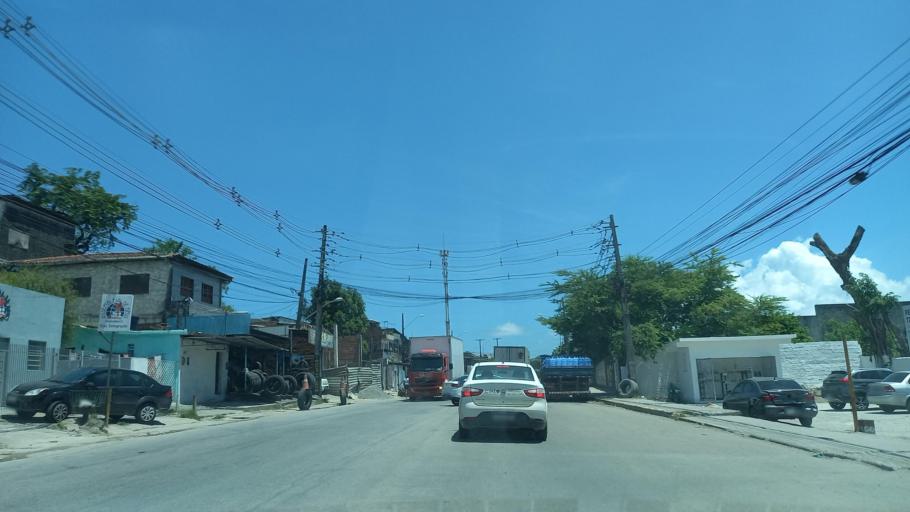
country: BR
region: Pernambuco
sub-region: Jaboatao Dos Guararapes
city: Jaboatao
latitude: -8.1548
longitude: -34.9444
